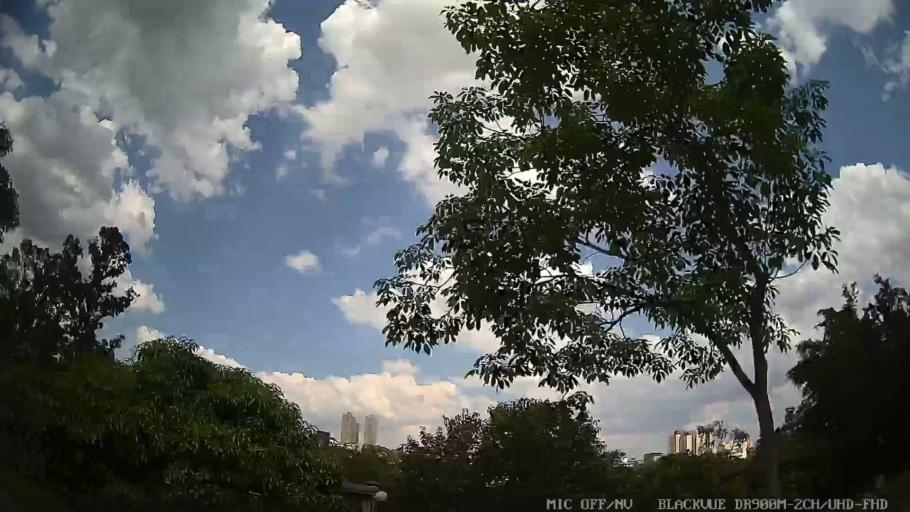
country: BR
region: Sao Paulo
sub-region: Ferraz De Vasconcelos
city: Ferraz de Vasconcelos
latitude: -23.5467
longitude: -46.4633
